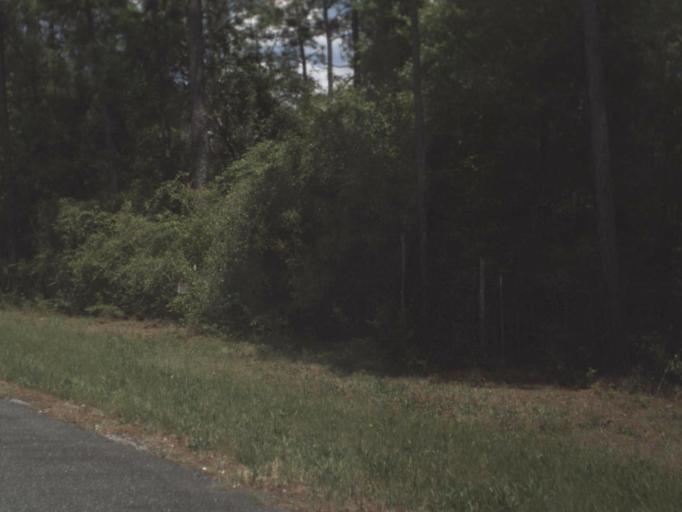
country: US
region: Florida
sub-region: Santa Rosa County
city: Point Baker
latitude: 30.7164
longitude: -87.0454
